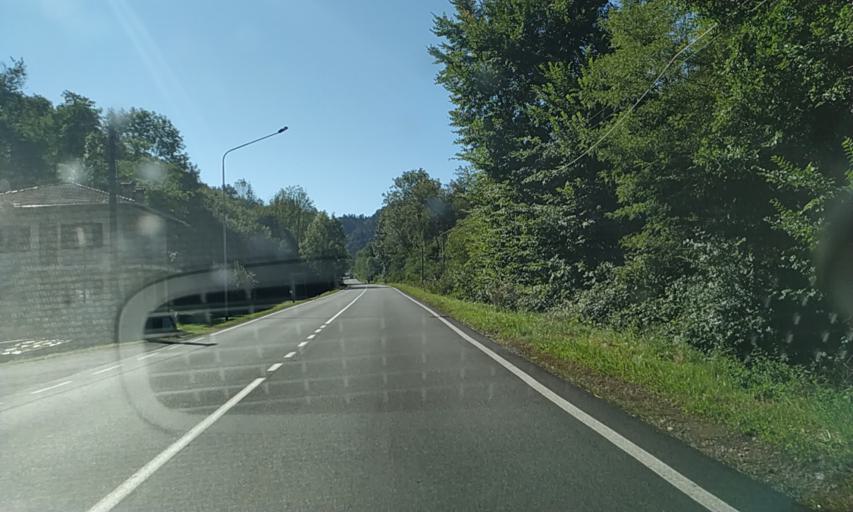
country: IT
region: Piedmont
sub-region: Provincia di Biella
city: Crevacuore
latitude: 45.6795
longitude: 8.2515
